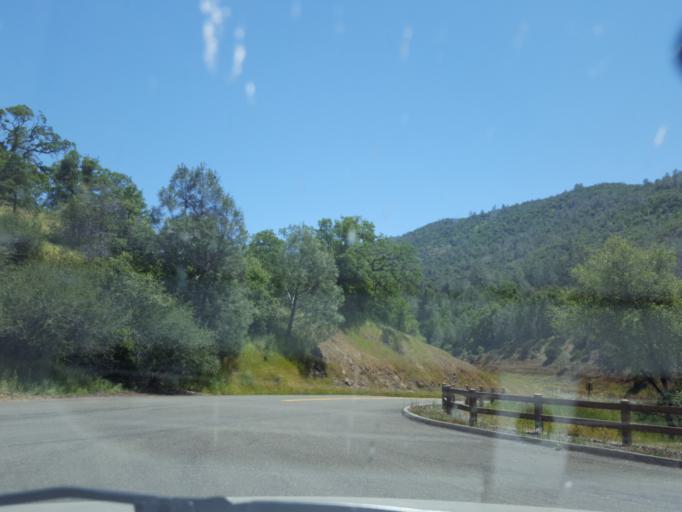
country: US
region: California
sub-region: Tuolumne County
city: Jamestown
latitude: 37.8319
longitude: -120.3489
